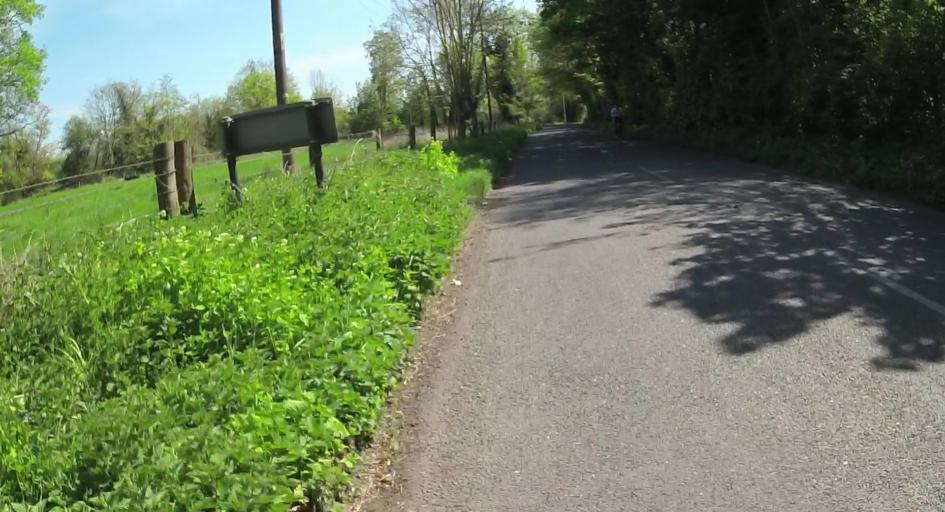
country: GB
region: England
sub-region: Hampshire
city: Andover
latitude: 51.1672
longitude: -1.4362
